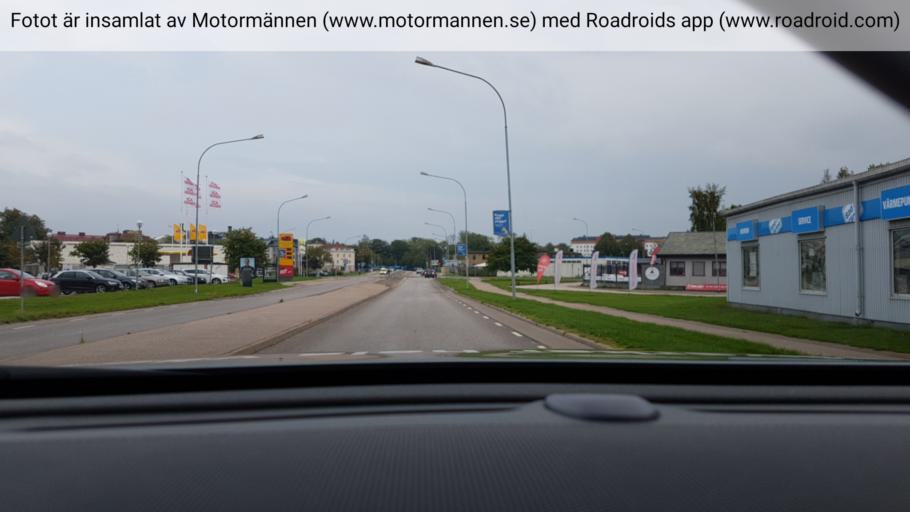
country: SE
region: Vaestra Goetaland
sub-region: Vanersborgs Kommun
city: Vanersborg
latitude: 58.3811
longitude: 12.3151
